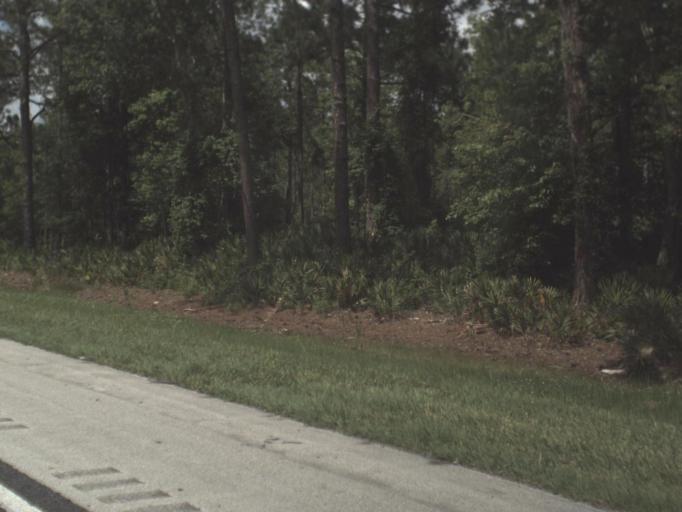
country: US
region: Florida
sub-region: Saint Johns County
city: Saint Augustine
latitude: 29.8754
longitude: -81.3991
